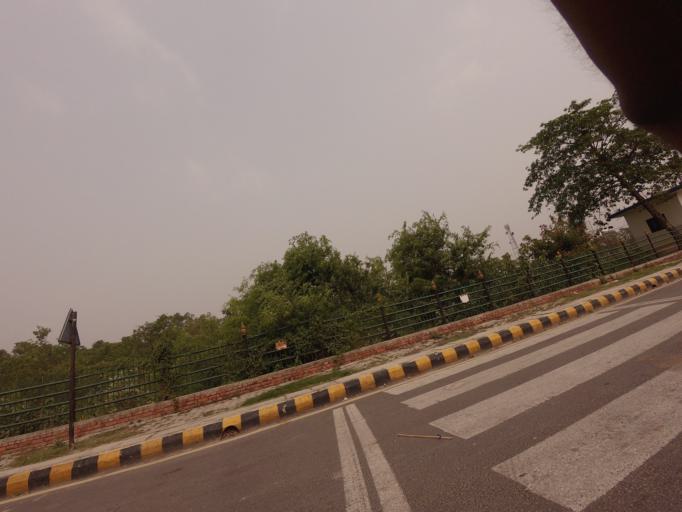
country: IN
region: Uttar Pradesh
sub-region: Maharajganj
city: Nautanwa
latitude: 27.4909
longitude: 83.2843
